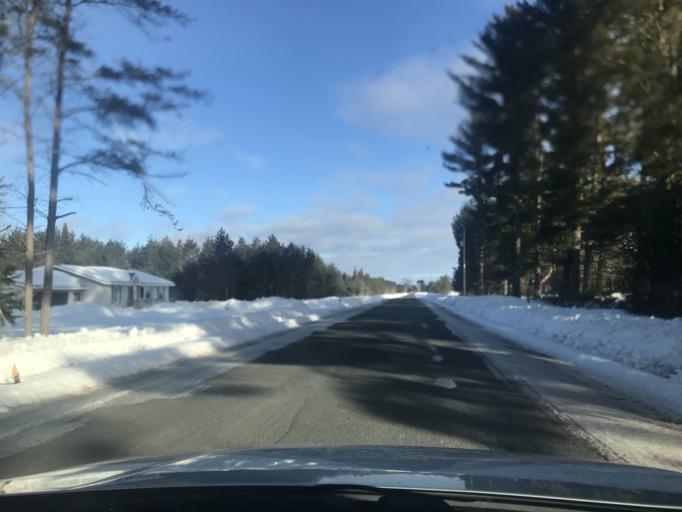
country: US
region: Wisconsin
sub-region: Marinette County
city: Niagara
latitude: 45.6110
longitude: -87.9769
